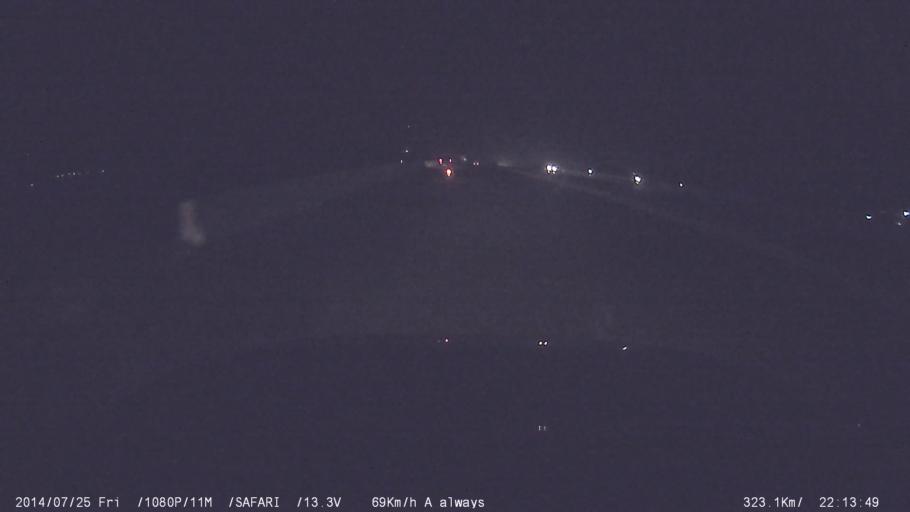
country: IN
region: Tamil Nadu
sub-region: Tiruppur
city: Avinashi
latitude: 11.1471
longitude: 77.2071
